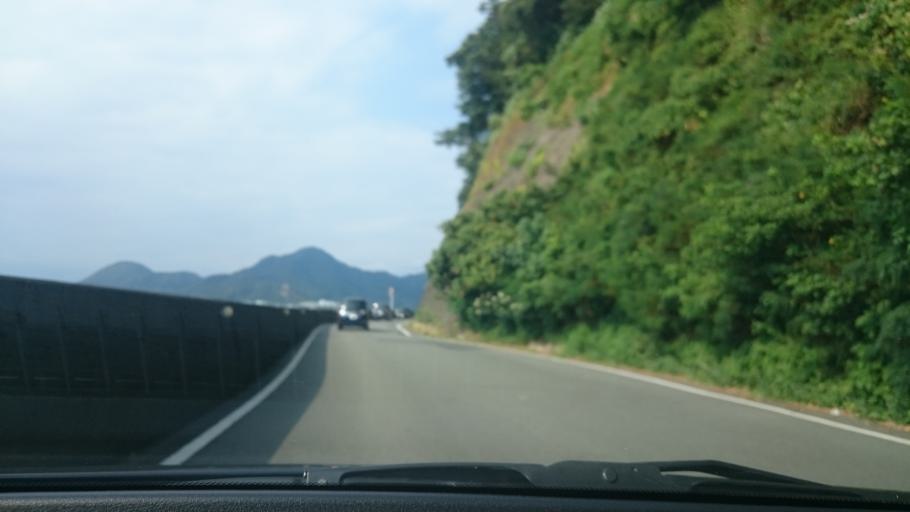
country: JP
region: Shizuoka
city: Numazu
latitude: 35.0236
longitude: 138.8726
